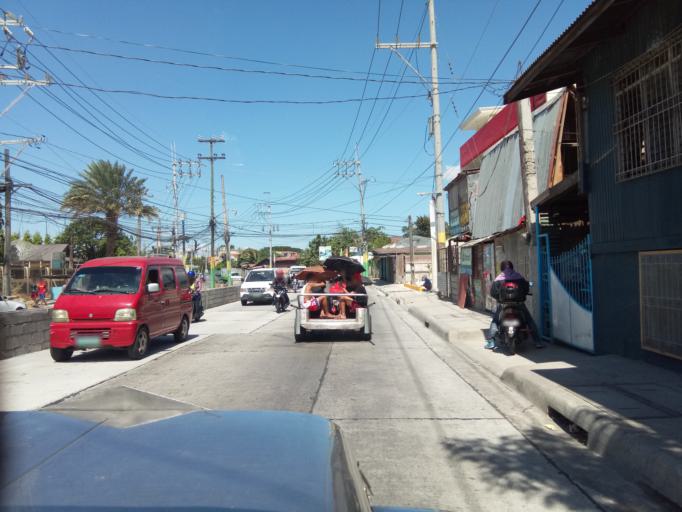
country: PH
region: Calabarzon
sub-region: Province of Cavite
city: Dasmarinas
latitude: 14.3505
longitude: 120.9417
